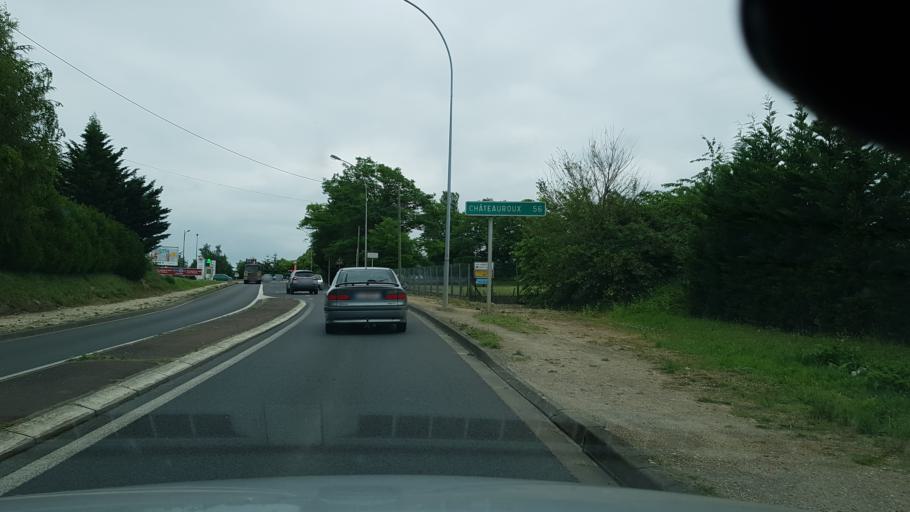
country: FR
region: Centre
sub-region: Departement du Loir-et-Cher
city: Selles-sur-Cher
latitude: 47.2840
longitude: 1.5403
